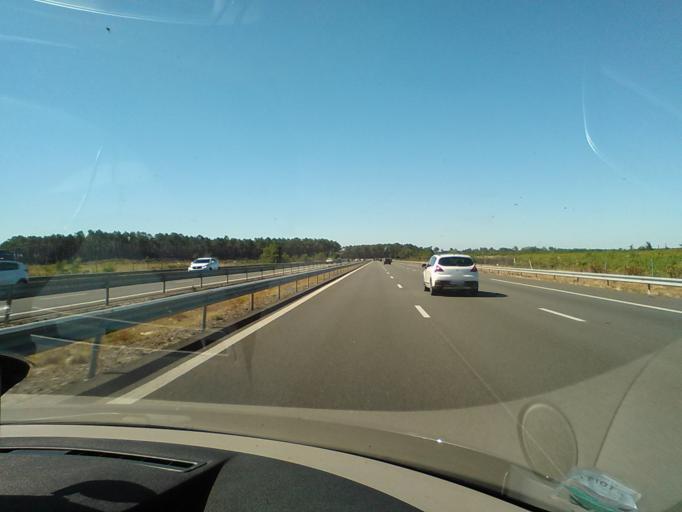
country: FR
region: Aquitaine
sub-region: Departement des Landes
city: Castets
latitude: 43.9015
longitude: -1.1293
